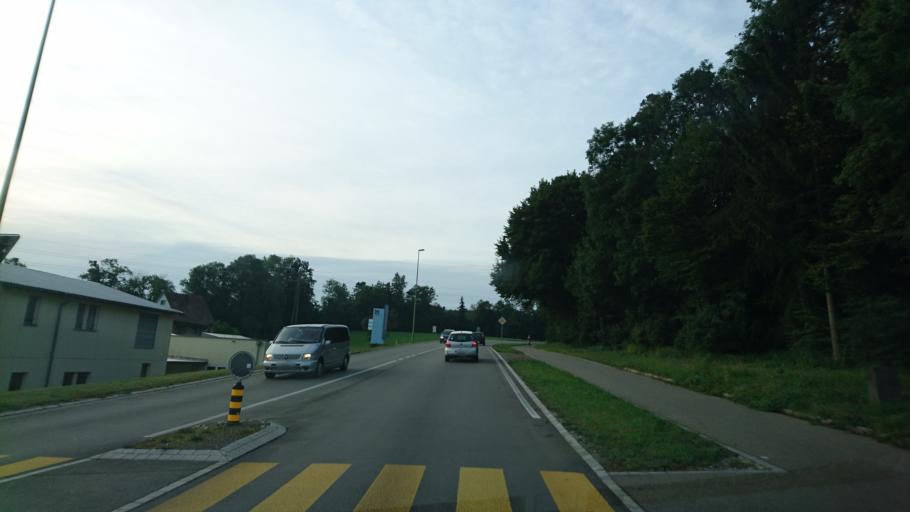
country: CH
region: Zurich
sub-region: Bezirk Uster
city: Moenchaltorf / Dorf
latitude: 47.3012
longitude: 8.7200
